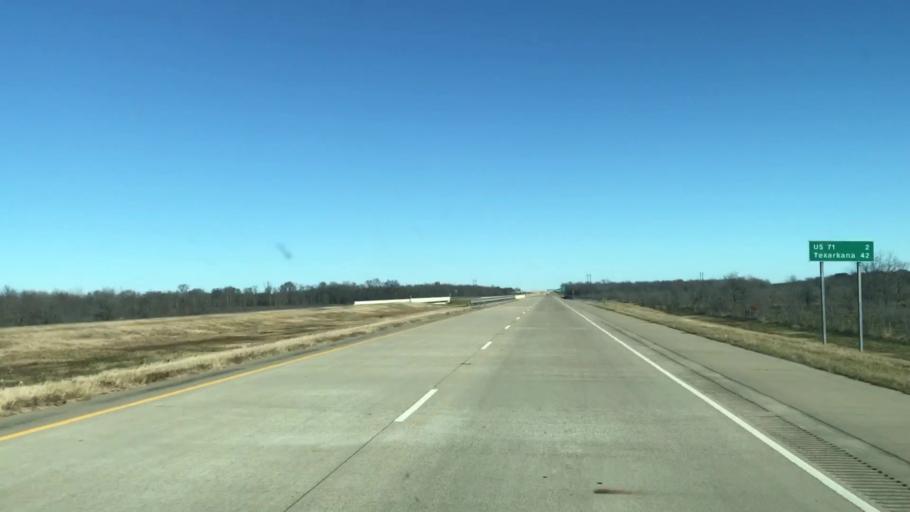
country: US
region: Louisiana
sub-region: Caddo Parish
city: Vivian
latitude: 32.8274
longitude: -93.8764
